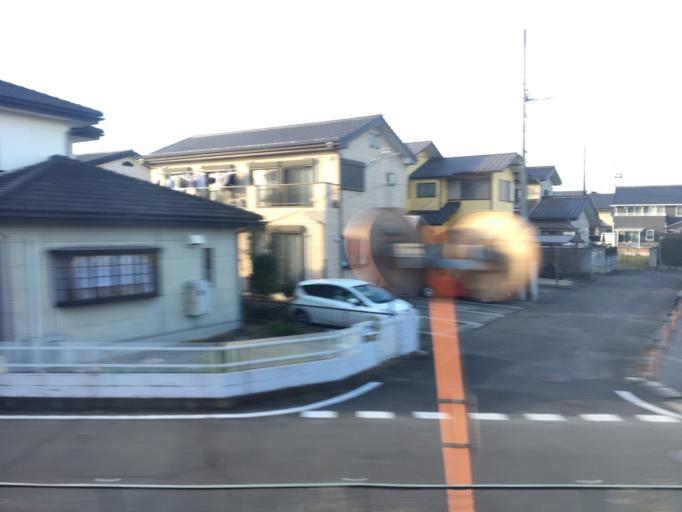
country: JP
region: Gunma
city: Omamacho-omama
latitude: 36.3859
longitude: 139.2814
